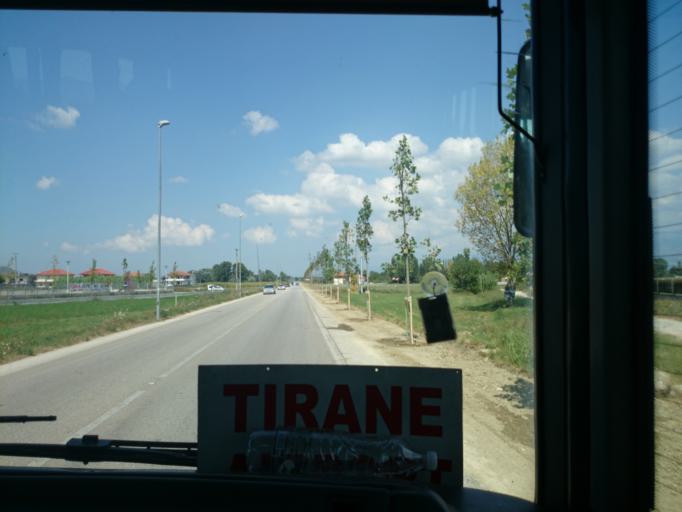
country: AL
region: Tirane
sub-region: Rrethi i Tiranes
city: Berxull
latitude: 41.3868
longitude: 19.7040
